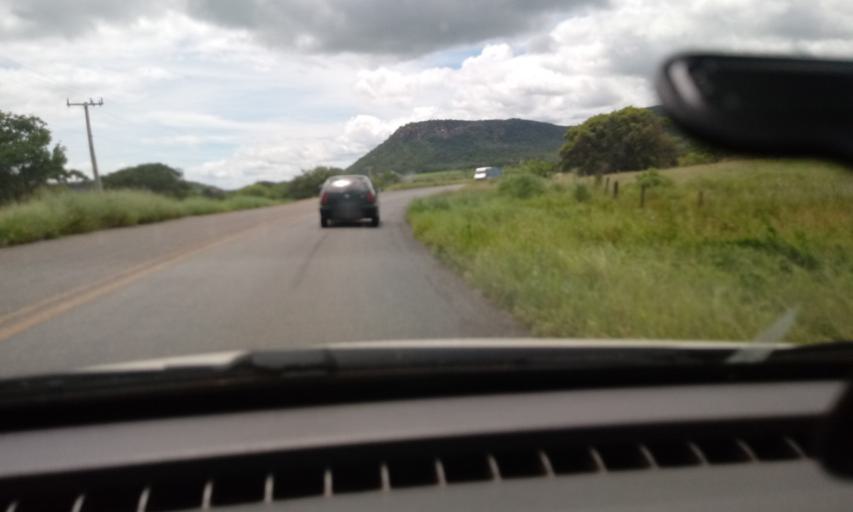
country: BR
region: Bahia
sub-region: Guanambi
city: Guanambi
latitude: -14.1524
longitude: -42.8255
